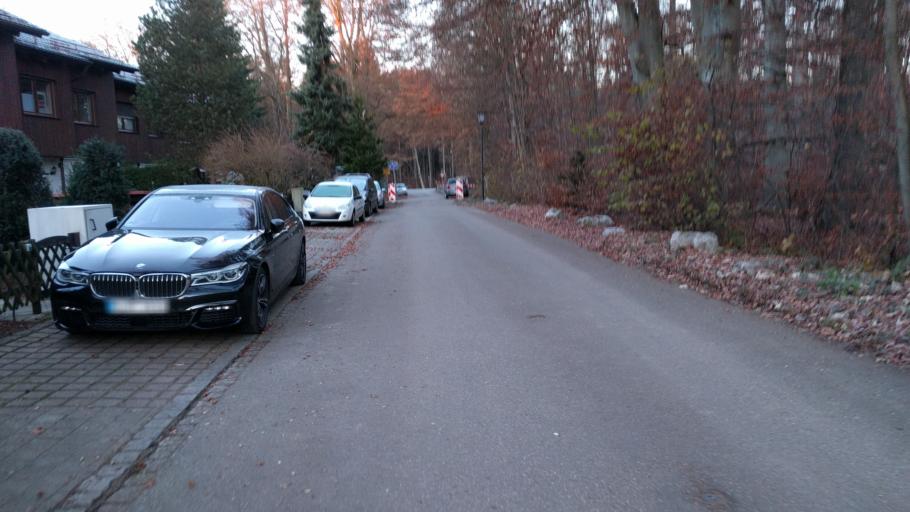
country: DE
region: Bavaria
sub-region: Upper Bavaria
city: Baierbrunn
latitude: 48.0340
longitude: 11.5009
